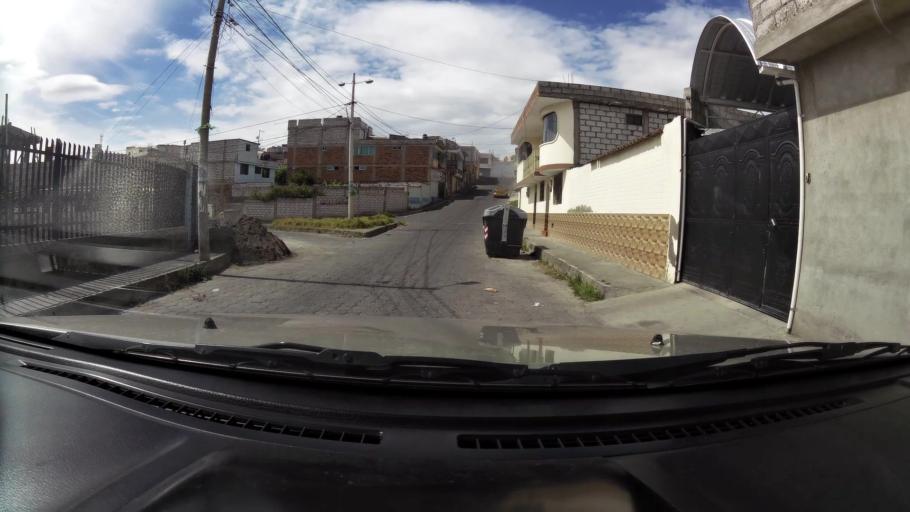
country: EC
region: Cotopaxi
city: Latacunga
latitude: -0.9356
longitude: -78.6078
